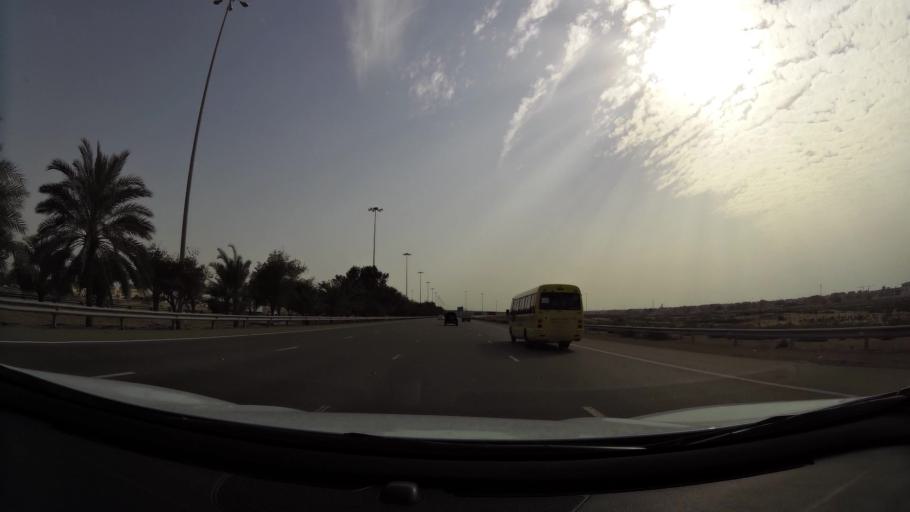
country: AE
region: Abu Dhabi
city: Abu Dhabi
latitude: 24.3749
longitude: 54.6568
